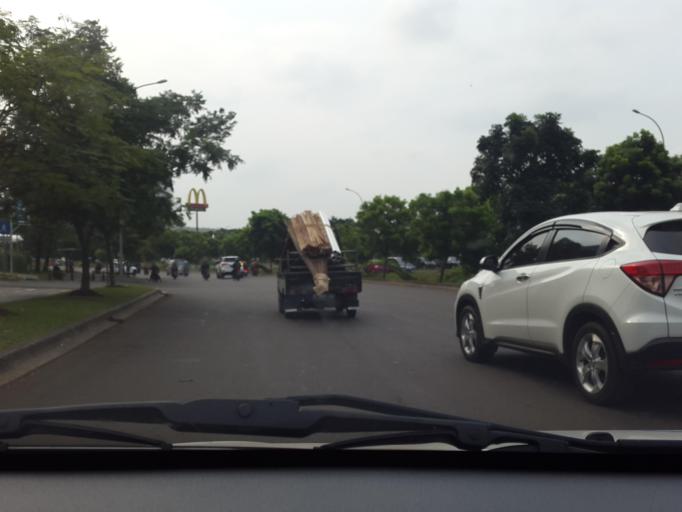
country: ID
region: Banten
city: South Tangerang
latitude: -6.2733
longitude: 106.6996
